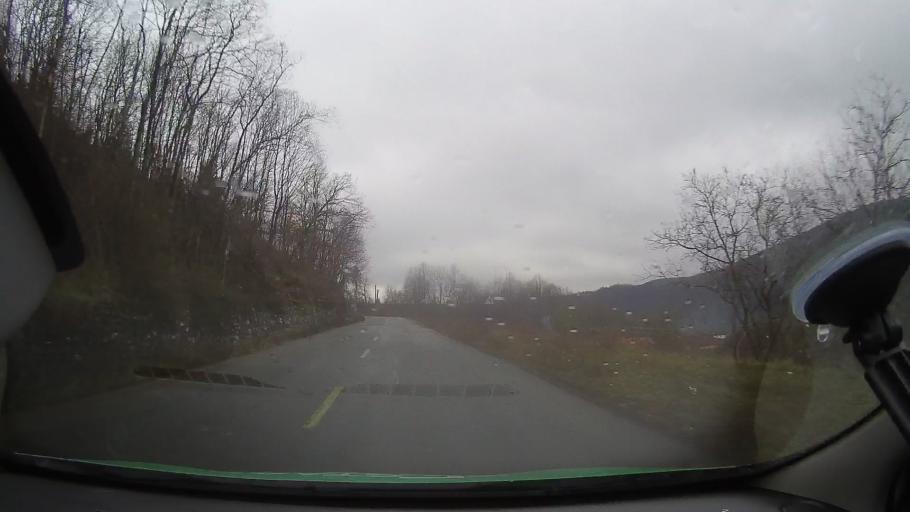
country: RO
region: Arad
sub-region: Comuna Halmagiu
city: Halmagiu
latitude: 46.2361
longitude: 22.5577
